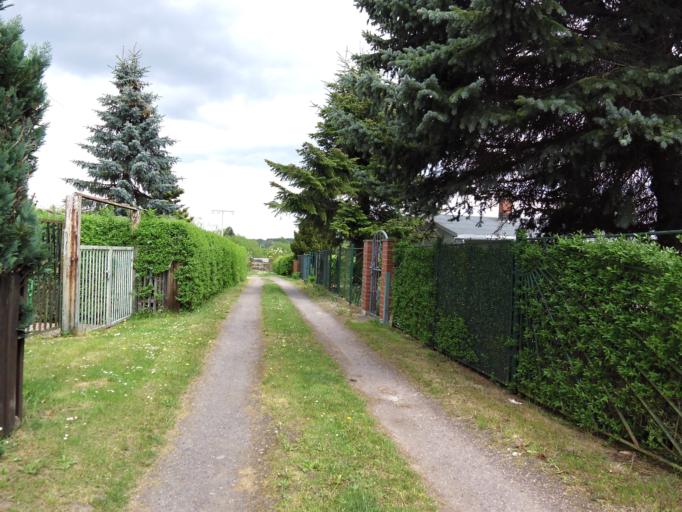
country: DE
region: Thuringia
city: Gotha
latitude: 50.9300
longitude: 10.7001
